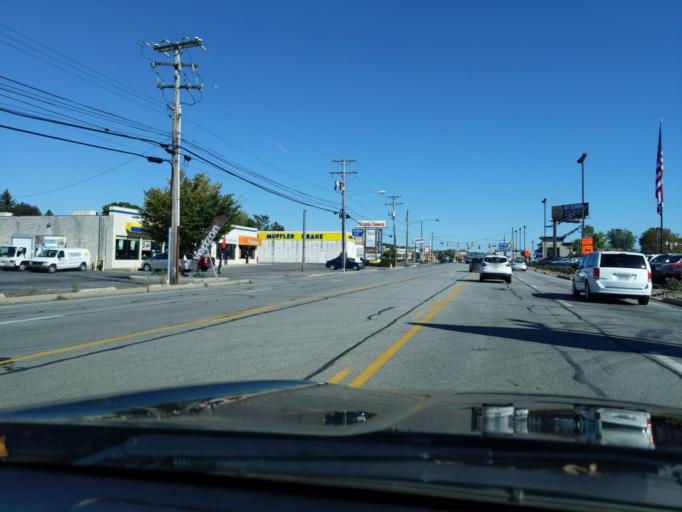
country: US
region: Pennsylvania
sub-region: Blair County
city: Lakemont
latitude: 40.4764
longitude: -78.4043
